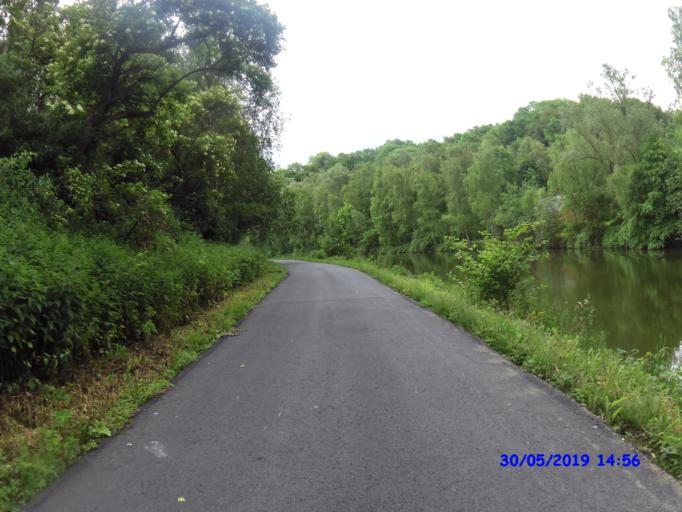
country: BE
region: Wallonia
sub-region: Province du Hainaut
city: Charleroi
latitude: 50.3886
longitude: 4.3744
